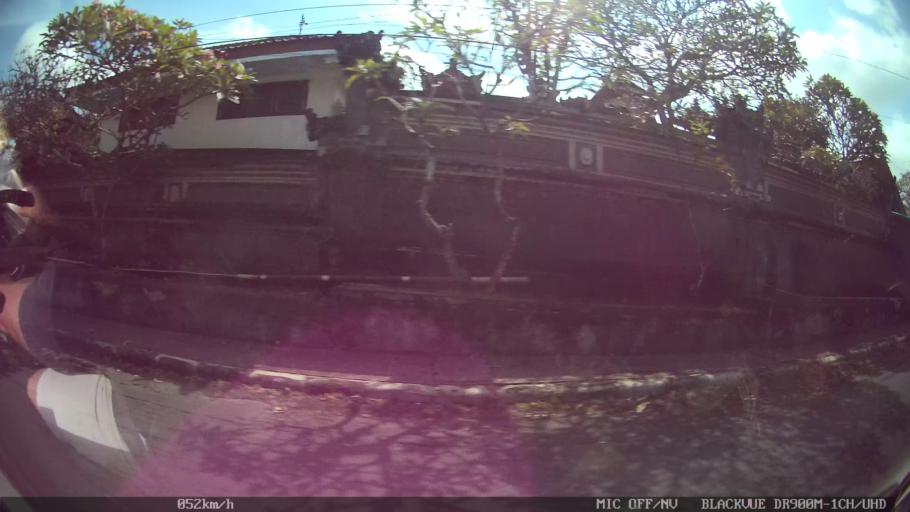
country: ID
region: Bali
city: Banjar Kelodan
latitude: -8.5293
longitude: 115.3287
